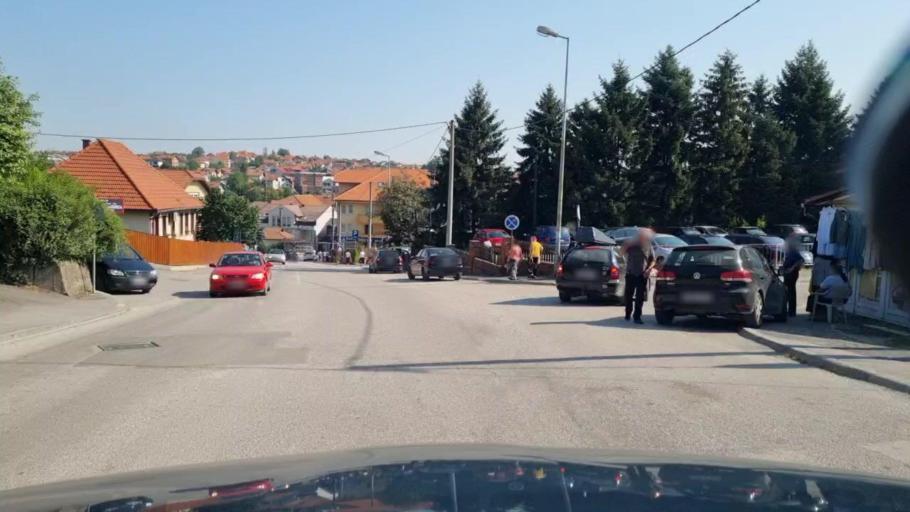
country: BA
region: Federation of Bosnia and Herzegovina
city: Gradacac
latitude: 44.8751
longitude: 18.4276
